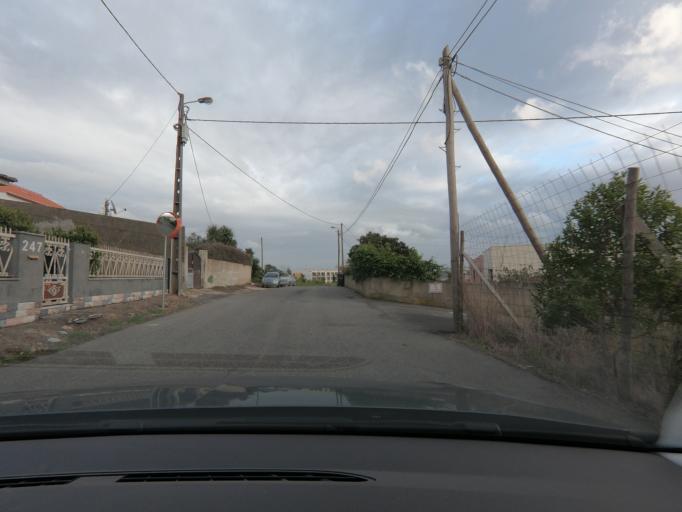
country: PT
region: Lisbon
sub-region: Cascais
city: Sao Domingos de Rana
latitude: 38.7298
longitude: -9.3269
